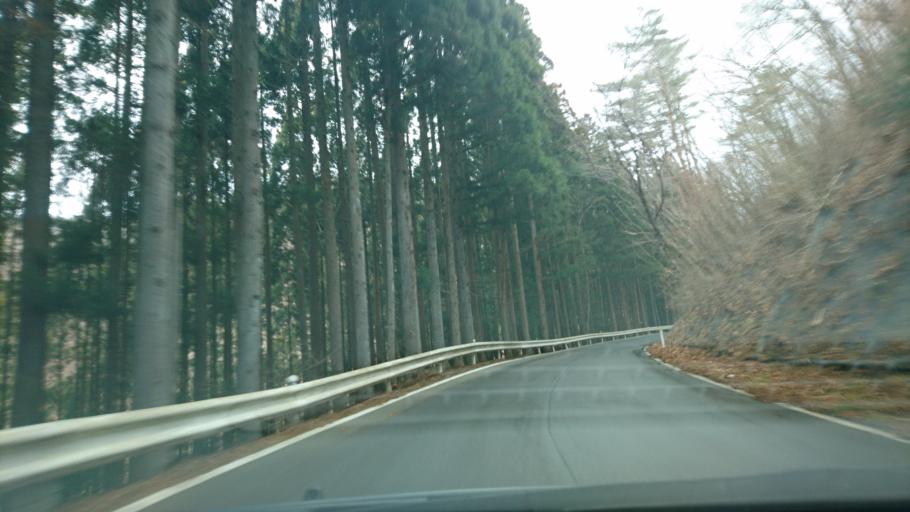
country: JP
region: Iwate
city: Ofunato
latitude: 38.9929
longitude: 141.5484
